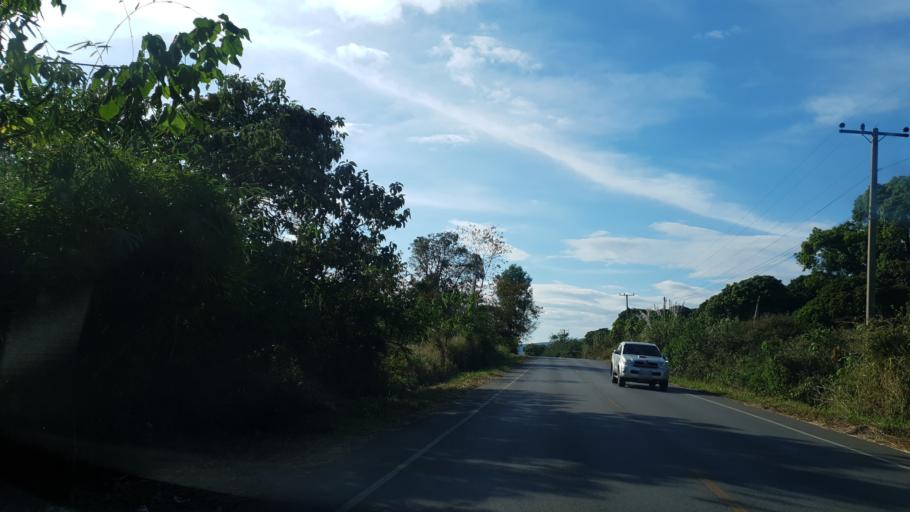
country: TH
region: Loei
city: Phu Ruea
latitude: 17.4461
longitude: 101.4960
